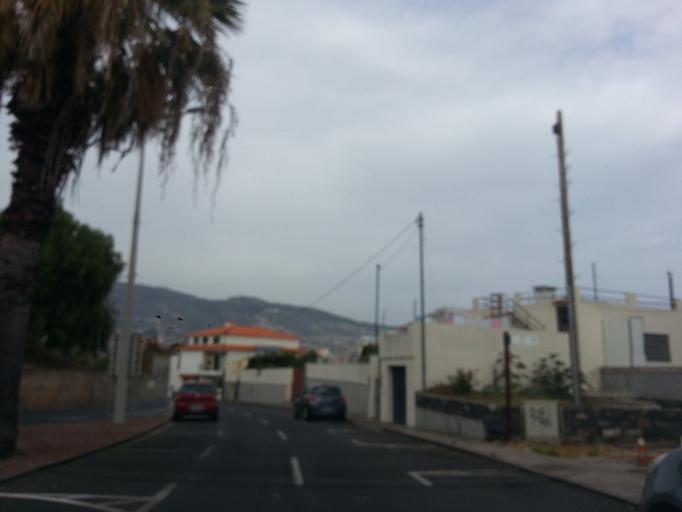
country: PT
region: Madeira
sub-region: Funchal
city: Funchal
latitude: 32.6446
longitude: -16.9324
